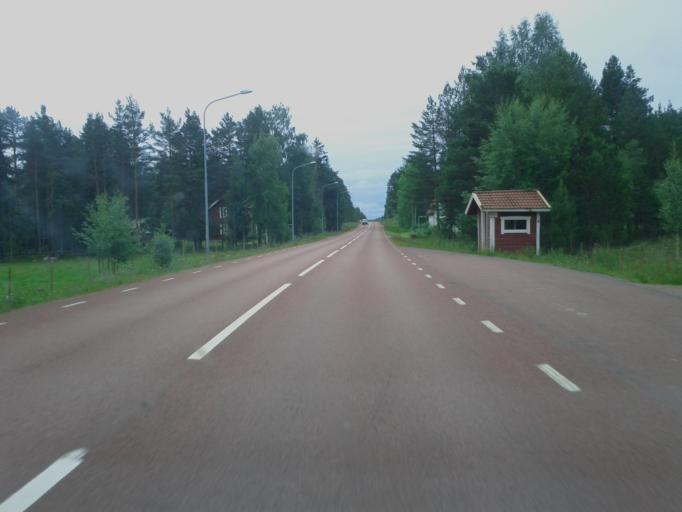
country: NO
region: Hedmark
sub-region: Trysil
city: Innbygda
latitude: 61.6881
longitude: 13.1629
